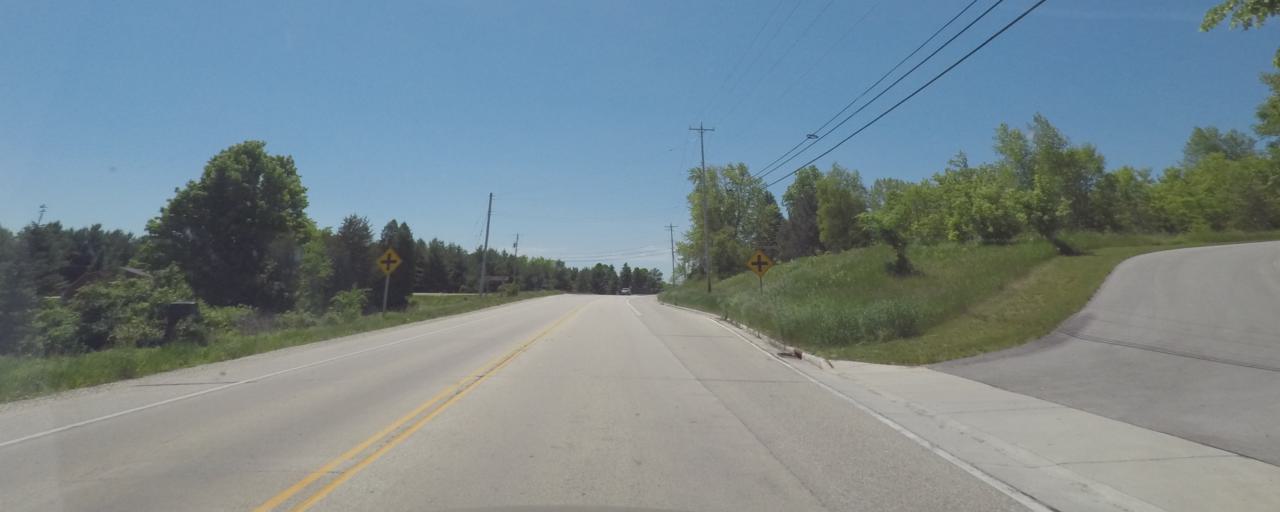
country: US
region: Wisconsin
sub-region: Washington County
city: West Bend
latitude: 43.4561
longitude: -88.1616
